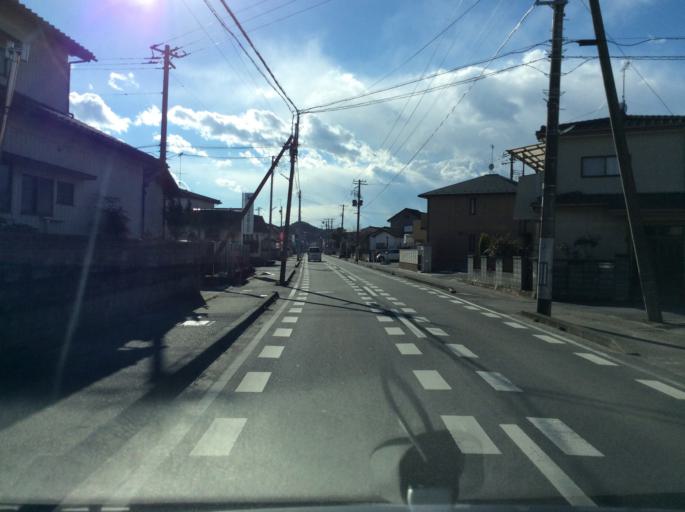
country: JP
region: Fukushima
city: Iwaki
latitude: 37.0678
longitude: 140.9414
